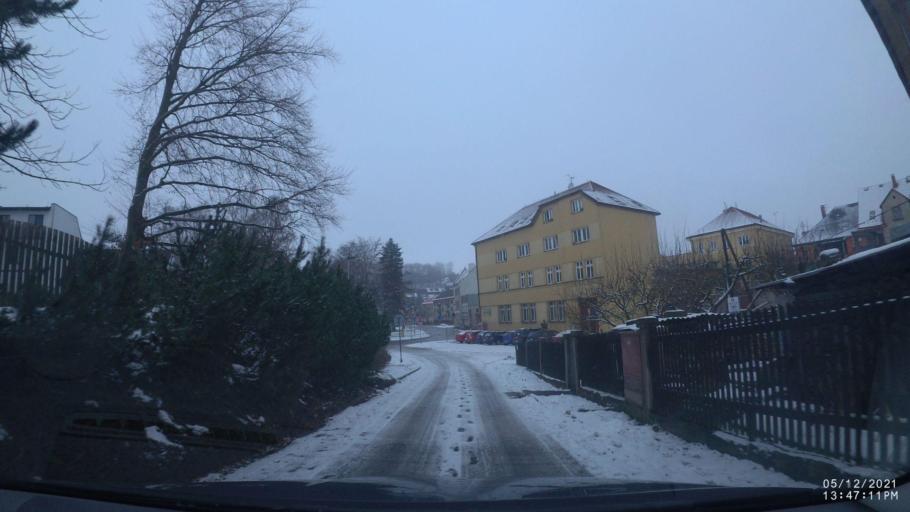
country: CZ
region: Kralovehradecky
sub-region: Okres Nachod
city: Police nad Metuji
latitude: 50.5352
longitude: 16.2344
